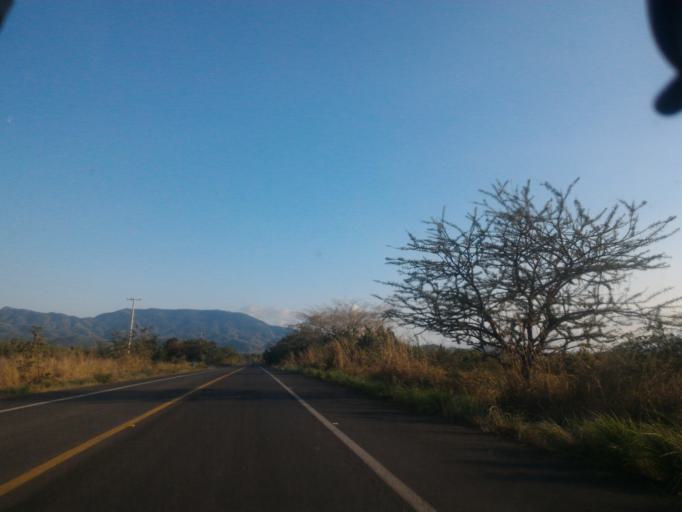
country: MX
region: Michoacan
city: Coahuayana Viejo
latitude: 18.6887
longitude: -103.6978
